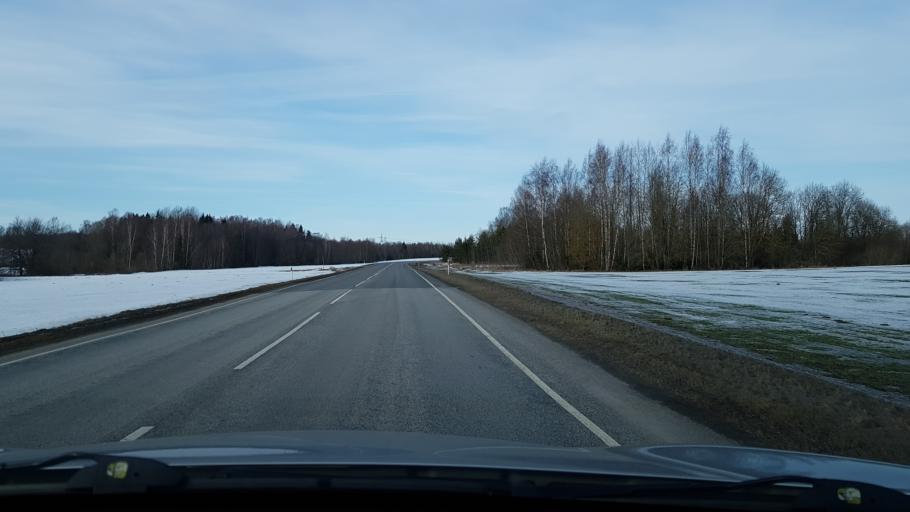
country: EE
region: Viljandimaa
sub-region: Viljandi linn
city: Viljandi
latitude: 58.3415
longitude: 25.4680
